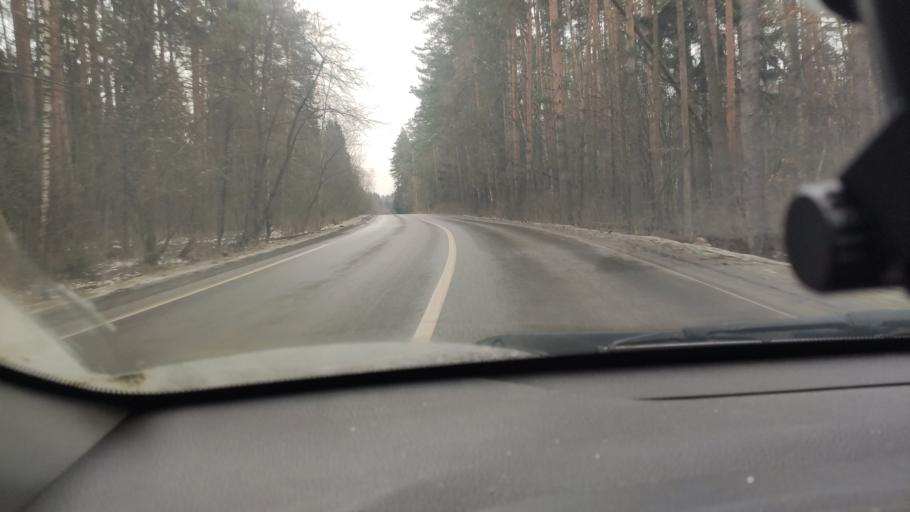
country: RU
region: Moskovskaya
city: Yakovlevskoye
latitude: 55.4562
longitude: 37.8703
